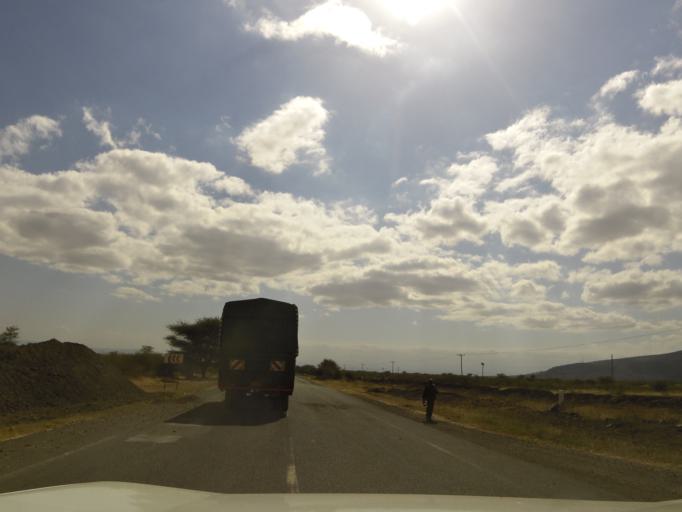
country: TZ
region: Arusha
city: Mto wa Mbu
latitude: -3.5096
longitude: 36.0187
